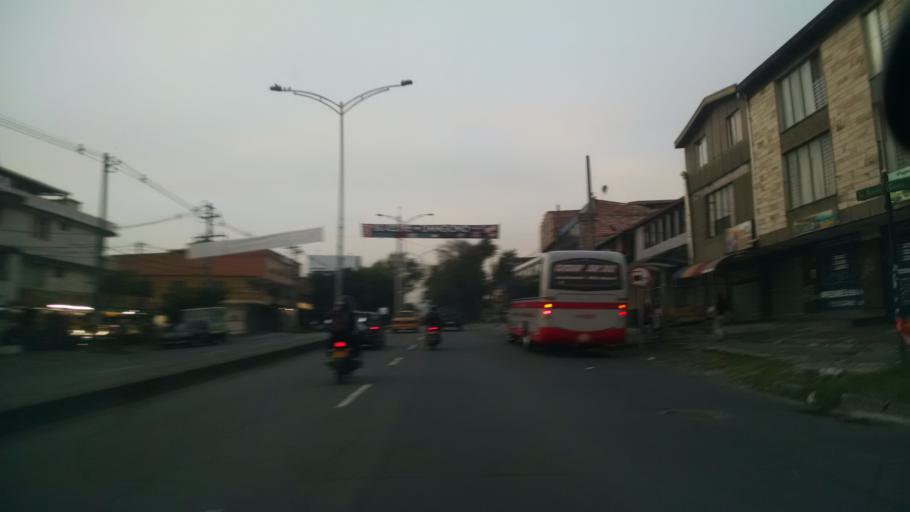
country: CO
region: Antioquia
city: Medellin
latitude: 6.2493
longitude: -75.6024
